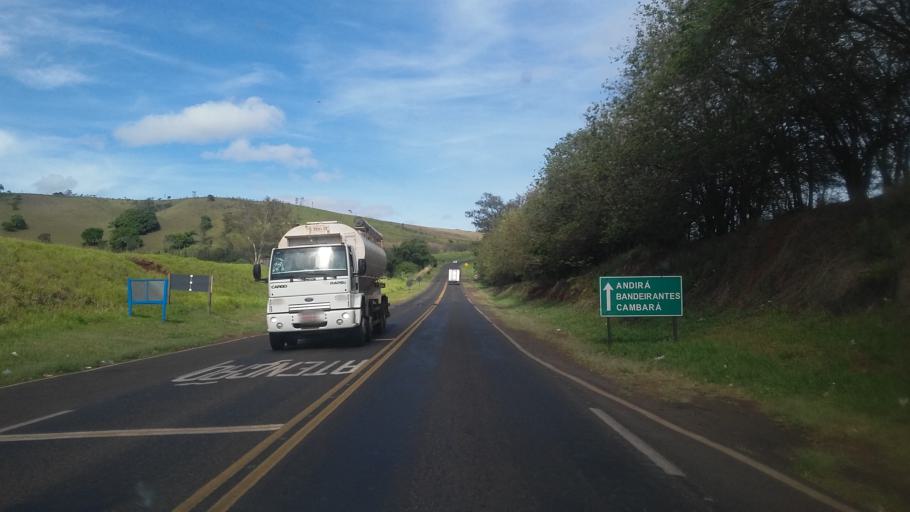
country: BR
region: Parana
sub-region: Santo Antonio Da Platina
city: Santo Antonio da Platina
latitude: -23.2760
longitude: -50.0718
